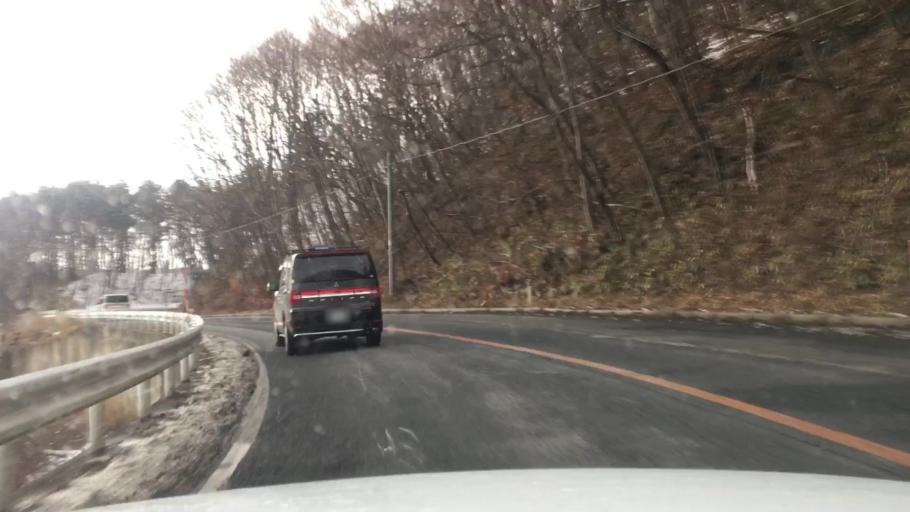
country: JP
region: Iwate
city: Morioka-shi
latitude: 39.6615
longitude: 141.3342
